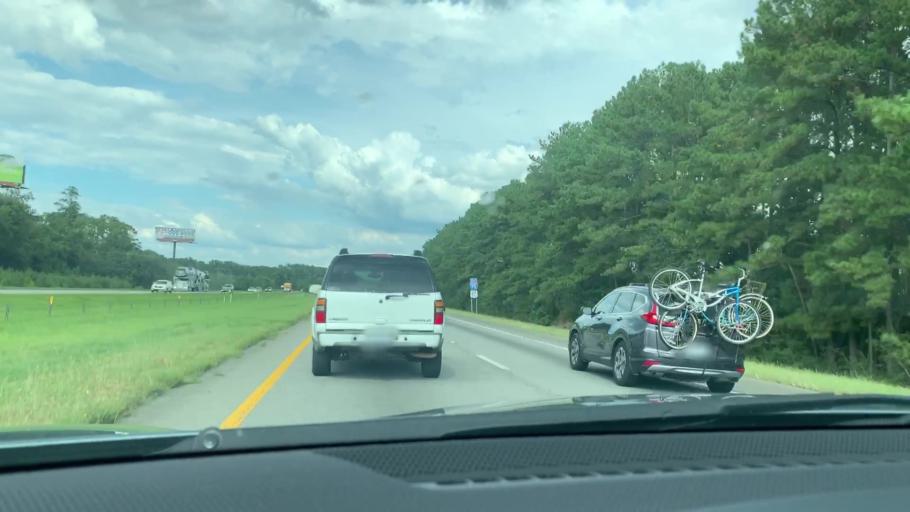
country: US
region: South Carolina
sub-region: Jasper County
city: Ridgeland
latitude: 32.5852
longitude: -80.9255
